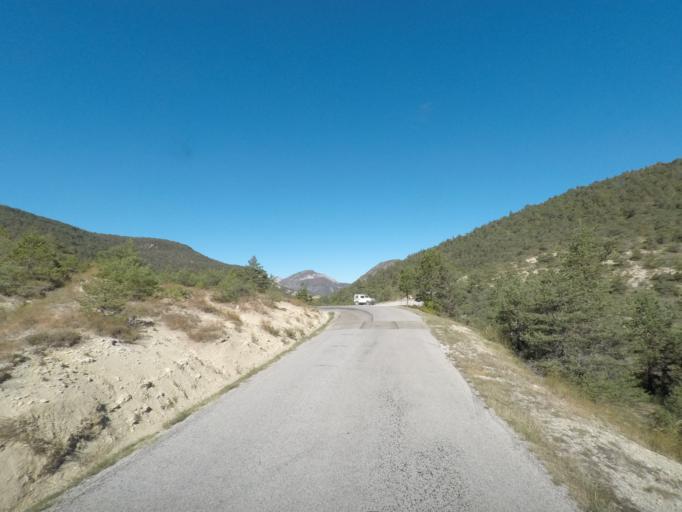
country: FR
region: Rhone-Alpes
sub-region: Departement de la Drome
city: Die
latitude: 44.5659
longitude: 5.3120
